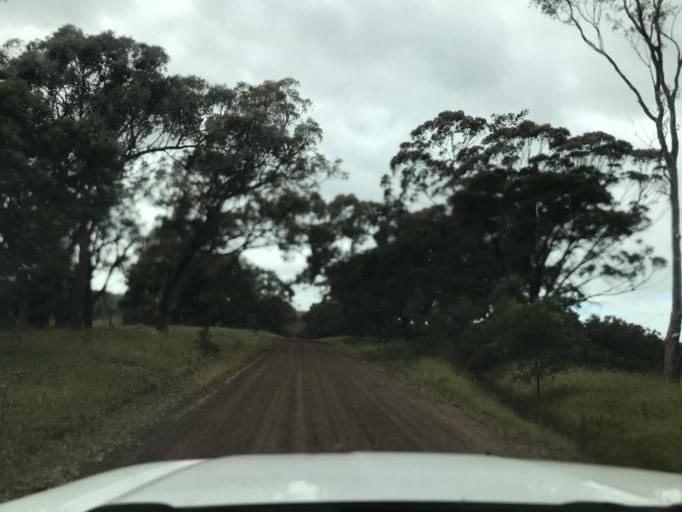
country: AU
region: South Australia
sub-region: Wattle Range
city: Penola
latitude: -37.3150
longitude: 141.4013
